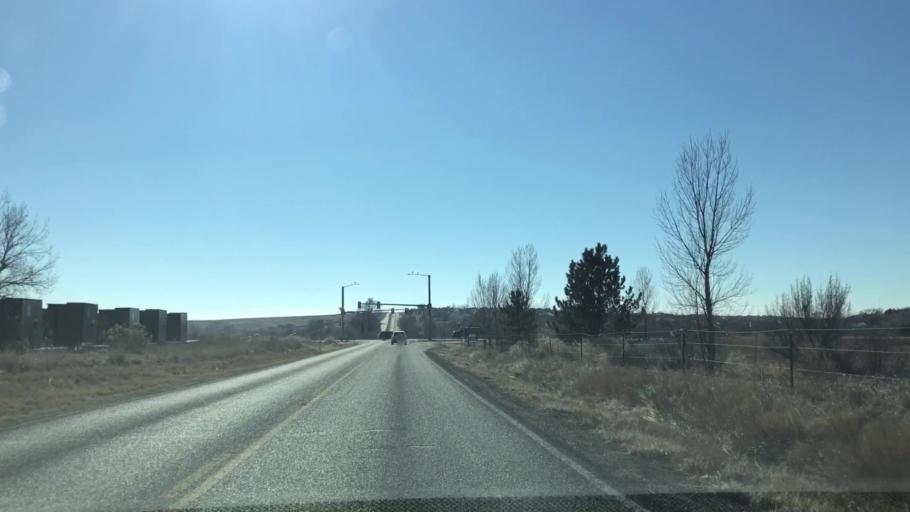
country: US
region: Colorado
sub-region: Weld County
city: Windsor
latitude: 40.4807
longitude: -104.9442
